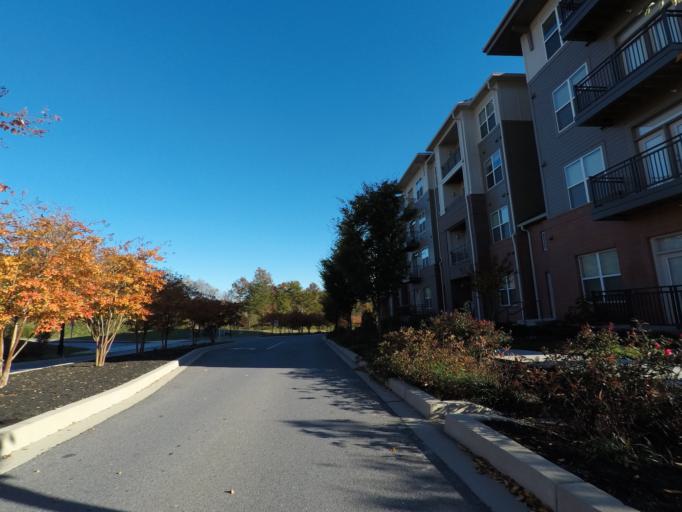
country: US
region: Maryland
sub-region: Howard County
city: Hanover
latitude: 39.1842
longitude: -76.7351
